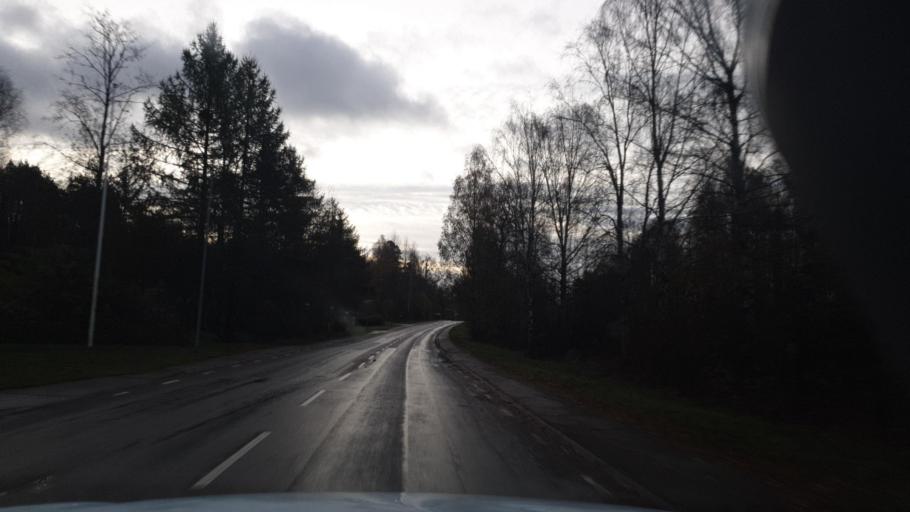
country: SE
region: Vaermland
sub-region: Arvika Kommun
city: Arvika
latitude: 59.6286
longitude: 12.8256
